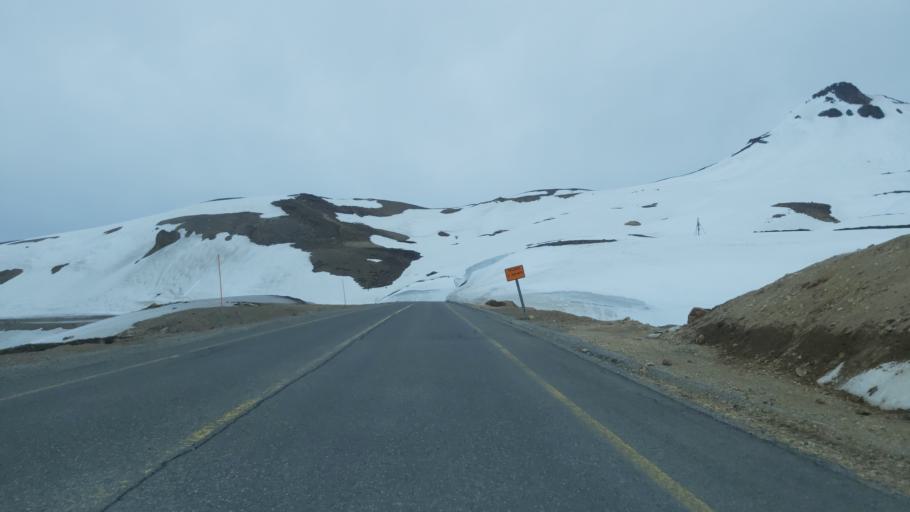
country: CL
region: Maule
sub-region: Provincia de Linares
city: Colbun
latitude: -36.0147
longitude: -70.4915
